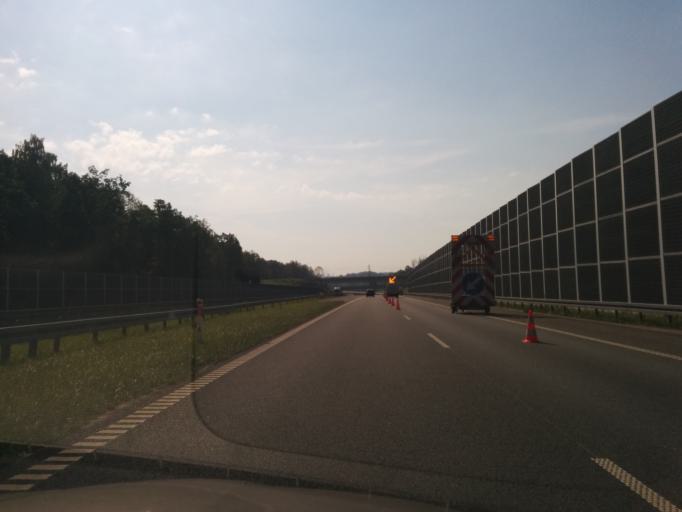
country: PL
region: Silesian Voivodeship
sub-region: Powiat tarnogorski
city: Radzionkow
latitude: 50.3772
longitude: 18.8742
